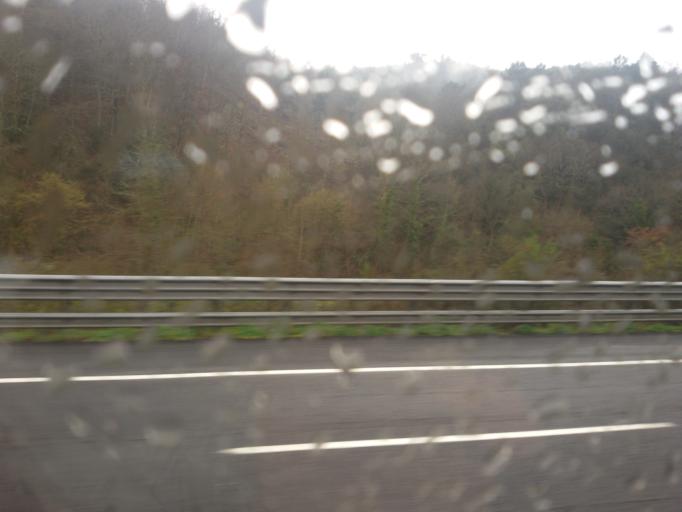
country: IT
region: Tuscany
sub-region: Province of Arezzo
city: Viciomaggio
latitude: 43.4467
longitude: 11.7666
